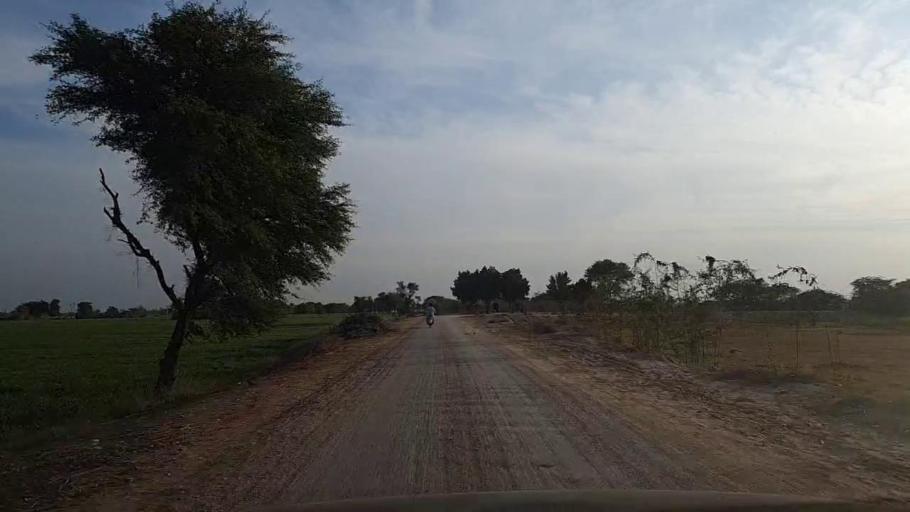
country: PK
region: Sindh
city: Jam Sahib
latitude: 26.4331
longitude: 68.5715
